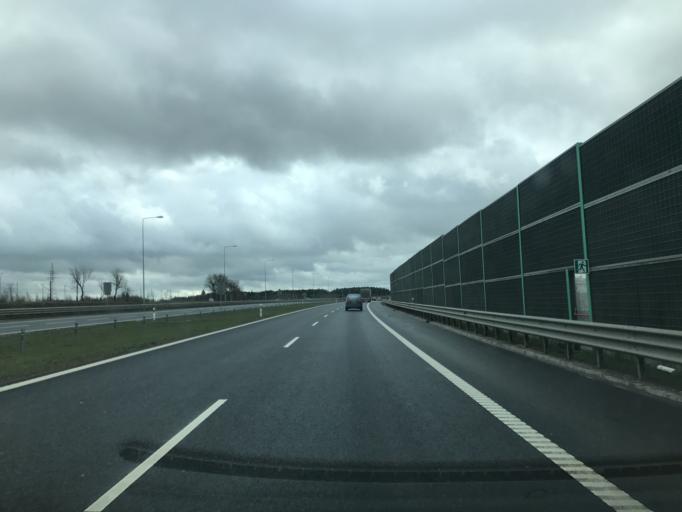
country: PL
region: Warmian-Masurian Voivodeship
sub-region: Powiat olsztynski
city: Olsztynek
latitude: 53.6062
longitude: 20.3146
